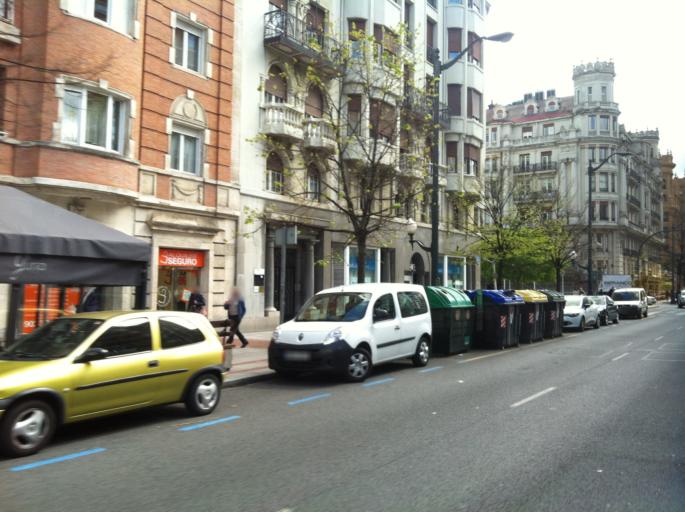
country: ES
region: Basque Country
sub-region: Bizkaia
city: Bilbao
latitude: 43.2647
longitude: -2.9419
